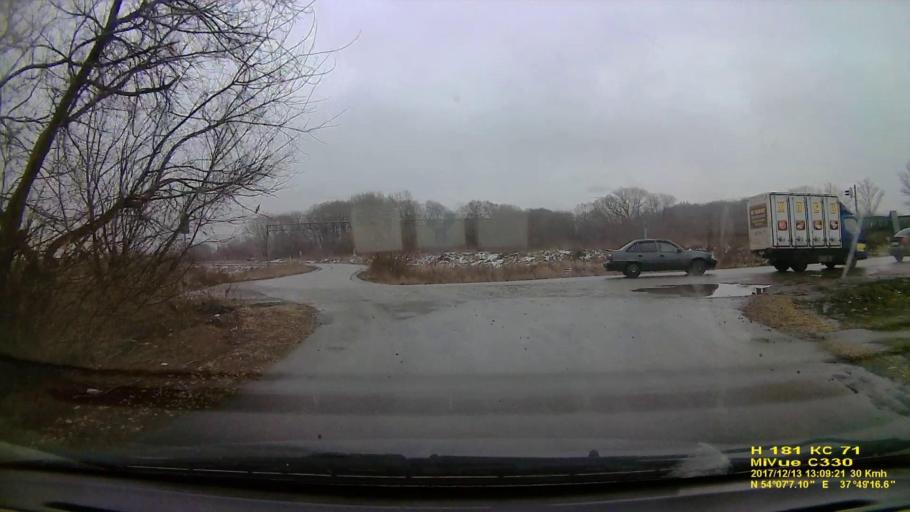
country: RU
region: Tula
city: Bolokhovo
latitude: 54.1186
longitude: 37.8214
